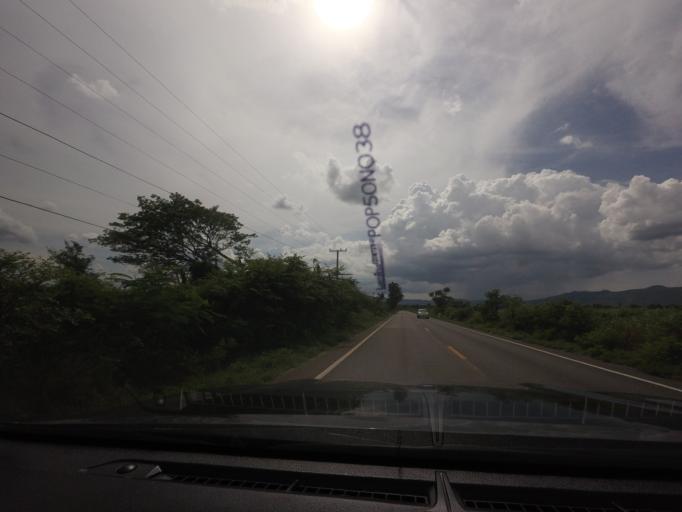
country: TH
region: Kanchanaburi
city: Bo Phloi
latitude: 14.1671
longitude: 99.4430
